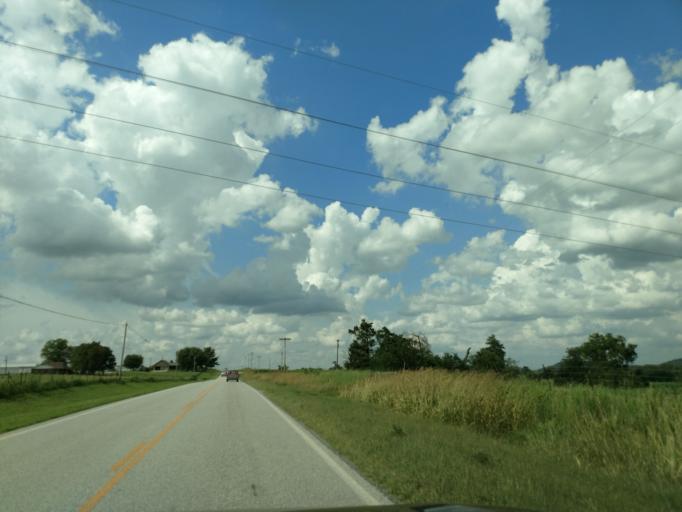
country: US
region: Arkansas
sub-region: Carroll County
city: Berryville
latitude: 36.4557
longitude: -93.5559
